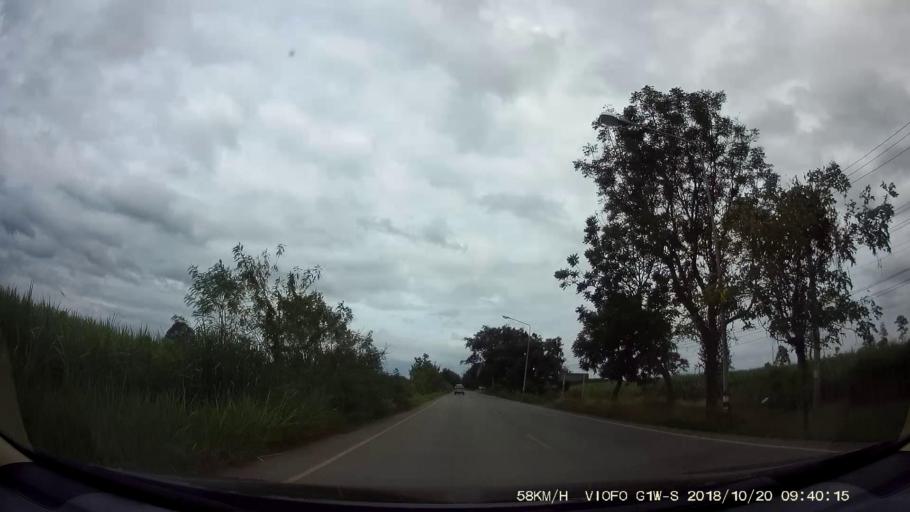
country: TH
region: Chaiyaphum
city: Kaset Sombun
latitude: 16.4412
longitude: 101.9623
